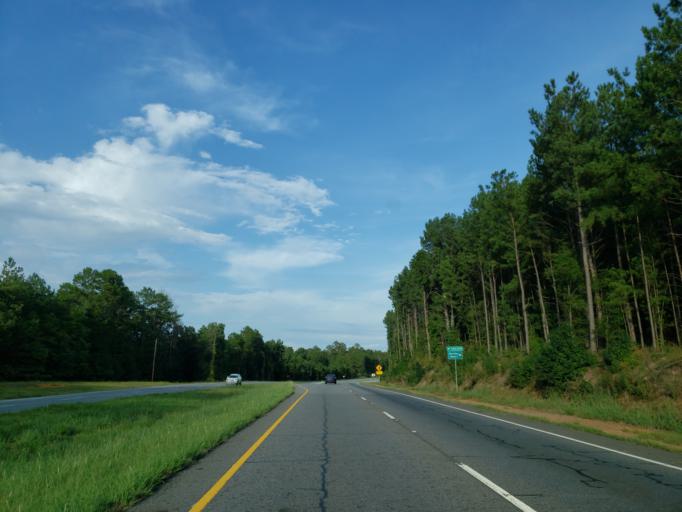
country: US
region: Georgia
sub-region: Bartow County
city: Euharlee
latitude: 34.2109
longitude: -84.9718
